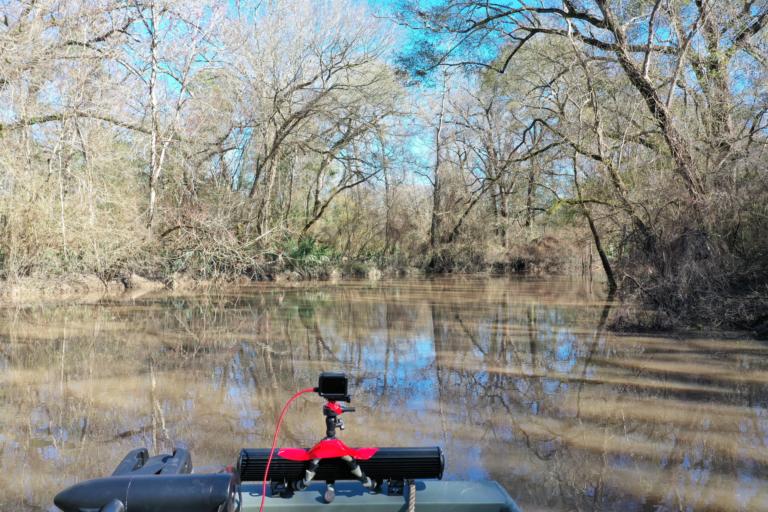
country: US
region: Louisiana
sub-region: Calcasieu Parish
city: Iowa
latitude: 30.3088
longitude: -93.0635
